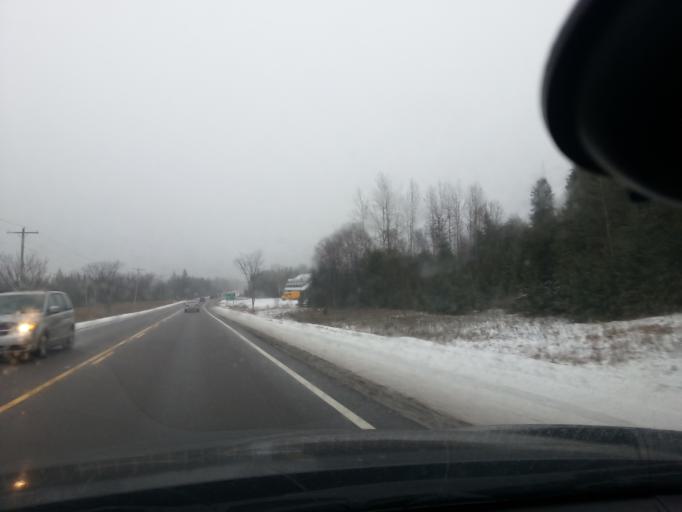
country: CA
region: Ontario
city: Skatepark
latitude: 44.7550
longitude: -76.8582
